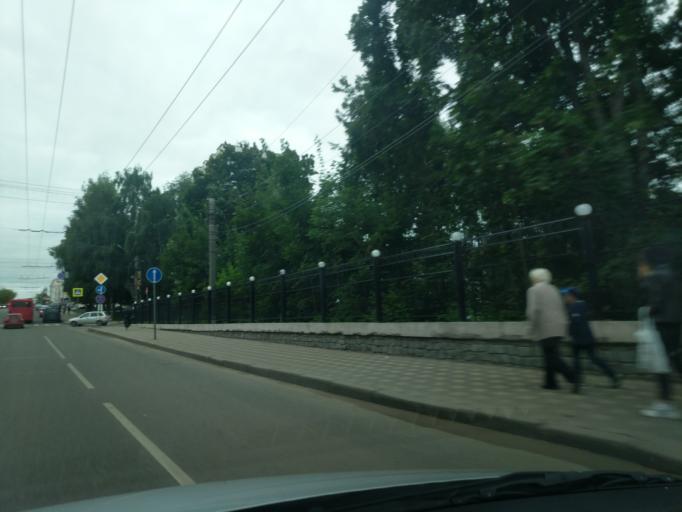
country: RU
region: Kirov
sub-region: Kirovo-Chepetskiy Rayon
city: Kirov
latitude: 58.5966
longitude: 49.6686
